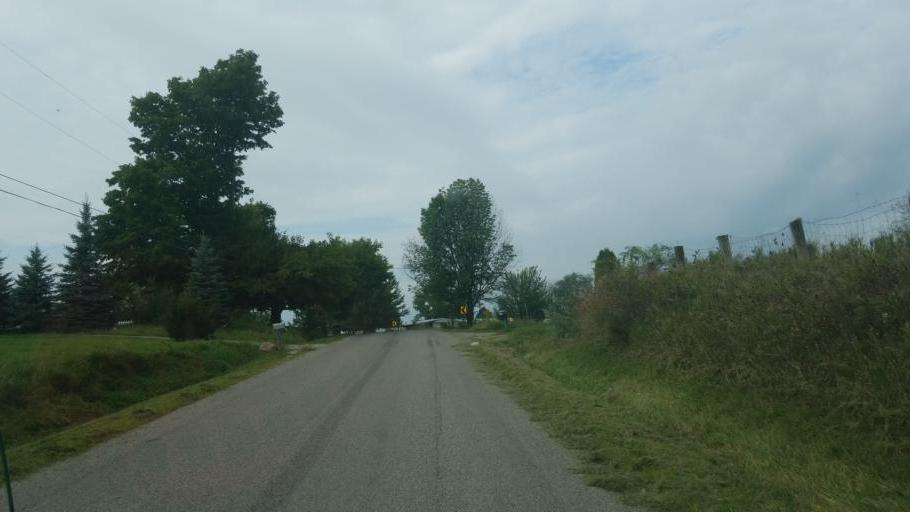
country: US
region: Ohio
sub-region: Wayne County
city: West Salem
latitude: 40.9352
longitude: -82.0559
